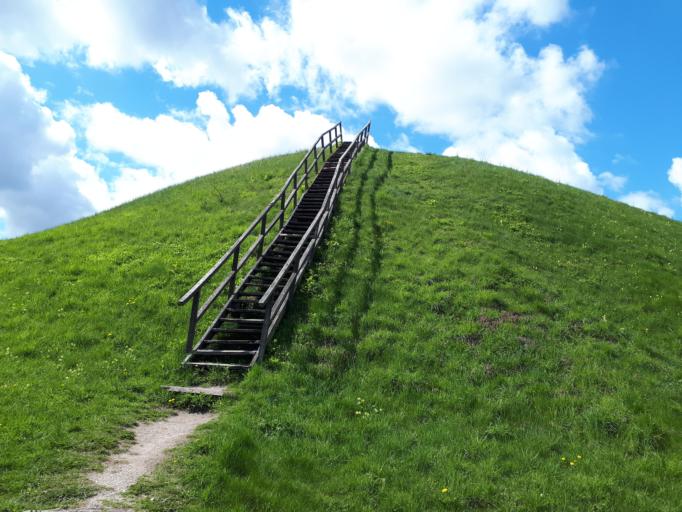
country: LT
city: Simnas
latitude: 54.3122
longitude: 23.6558
